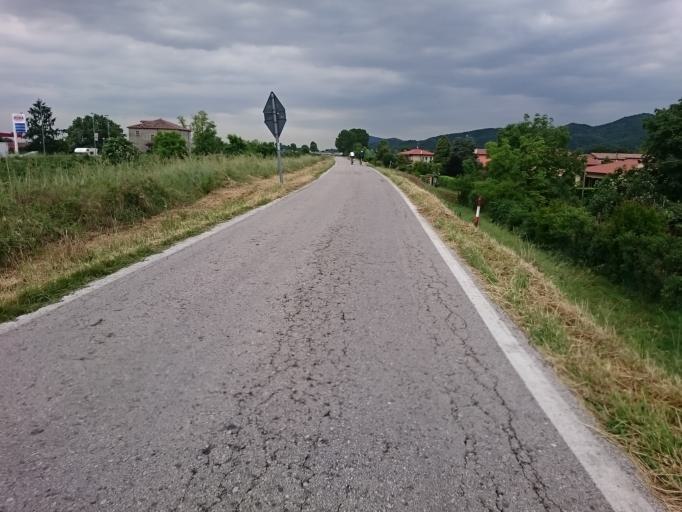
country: IT
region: Veneto
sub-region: Provincia di Padova
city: Terradura
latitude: 45.3219
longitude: 11.8094
